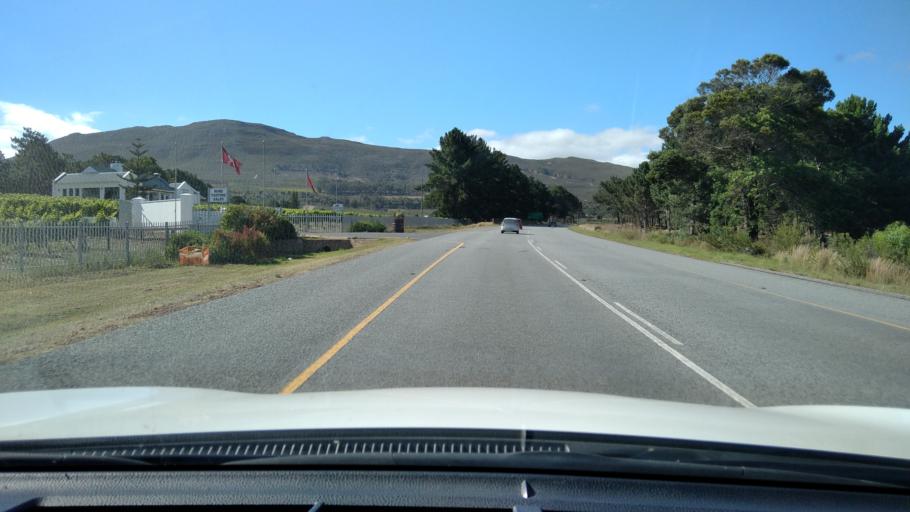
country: ZA
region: Western Cape
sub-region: Overberg District Municipality
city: Hermanus
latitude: -34.3039
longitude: 19.1442
